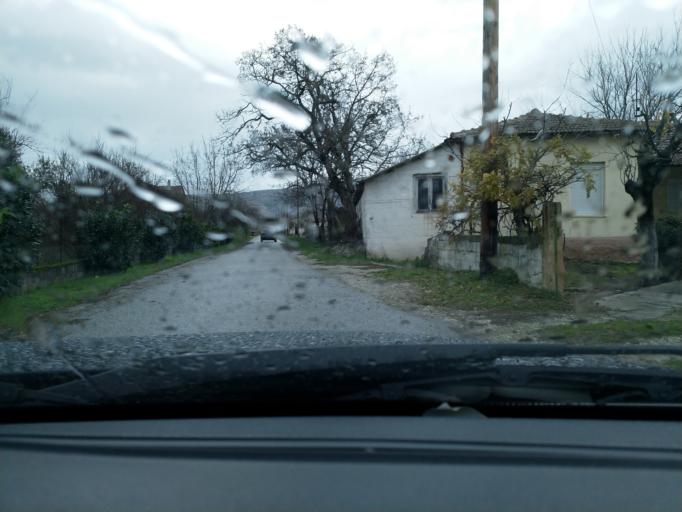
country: GR
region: Thessaly
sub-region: Trikala
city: Taxiarches
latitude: 39.5472
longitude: 21.8957
